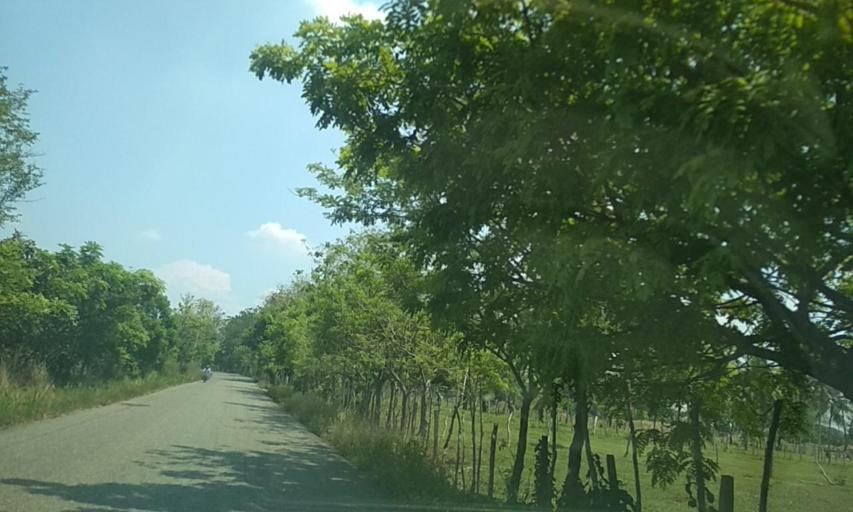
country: MX
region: Tabasco
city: Huimanguillo
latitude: 17.8208
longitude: -93.5030
